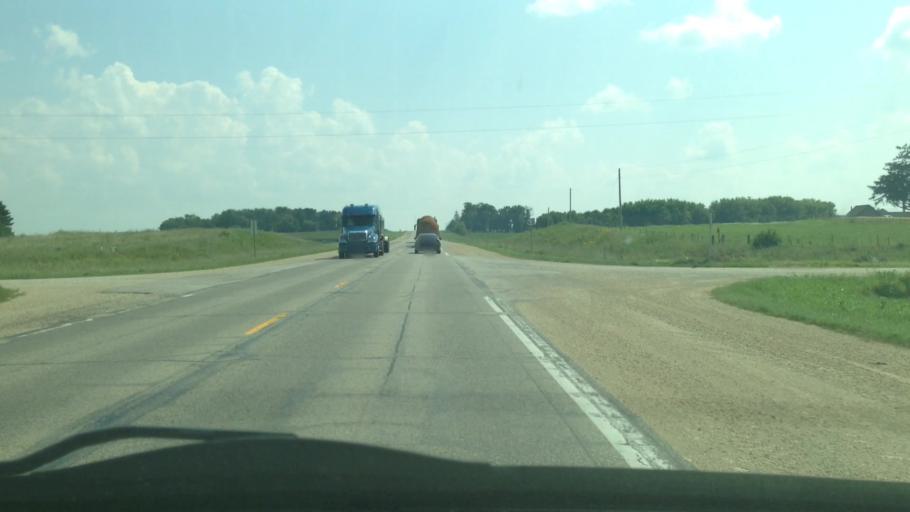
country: US
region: Iowa
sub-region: Chickasaw County
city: New Hampton
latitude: 43.2277
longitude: -92.2986
